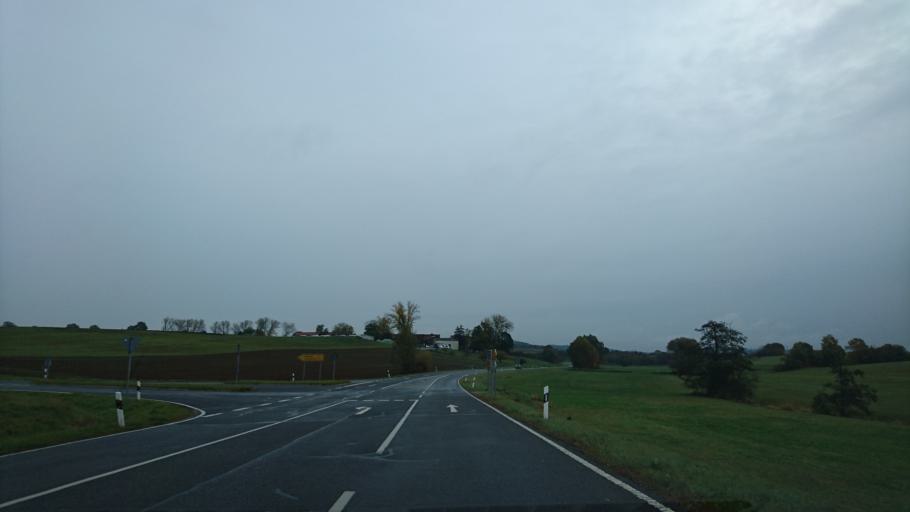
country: DE
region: Bavaria
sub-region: Regierungsbezirk Mittelfranken
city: Heideck
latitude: 49.1112
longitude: 11.1671
